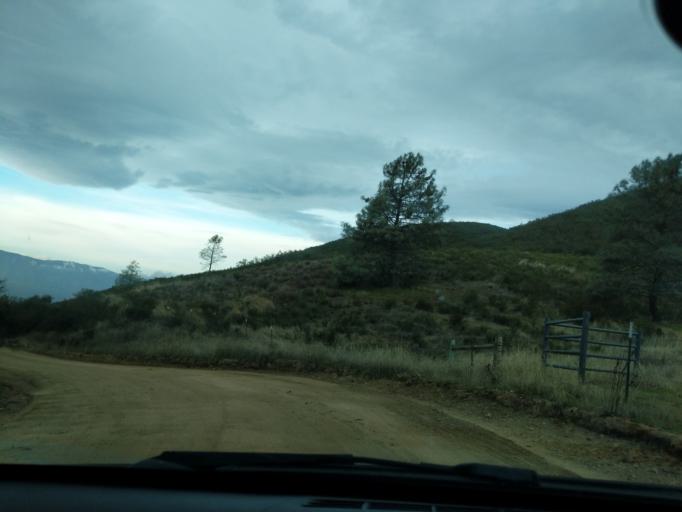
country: US
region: California
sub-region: Monterey County
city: Soledad
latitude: 36.5380
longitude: -121.3006
